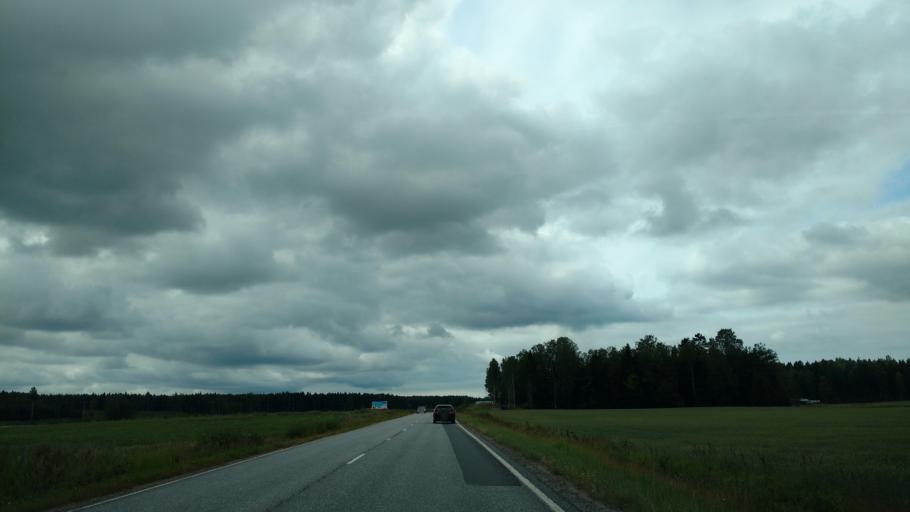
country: FI
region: Varsinais-Suomi
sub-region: Aboland-Turunmaa
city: Vaestanfjaerd
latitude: 60.1070
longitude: 22.5943
